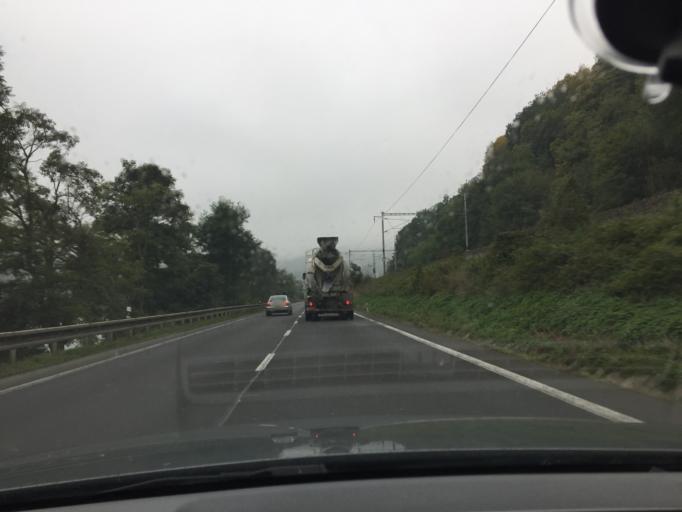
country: CZ
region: Ustecky
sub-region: Okres Usti nad Labem
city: Usti nad Labem
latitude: 50.6013
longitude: 14.0702
